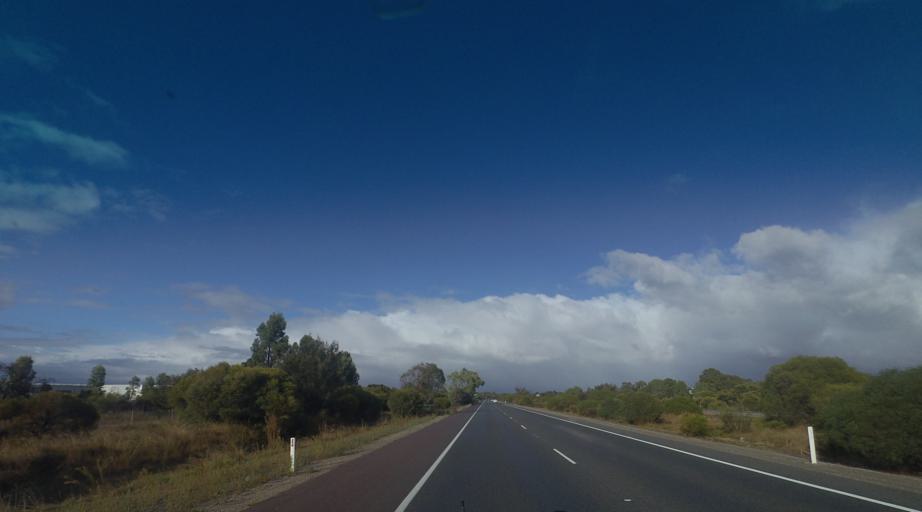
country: AU
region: Western Australia
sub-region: Armadale
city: Seville Grove
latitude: -32.1365
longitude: 115.9594
